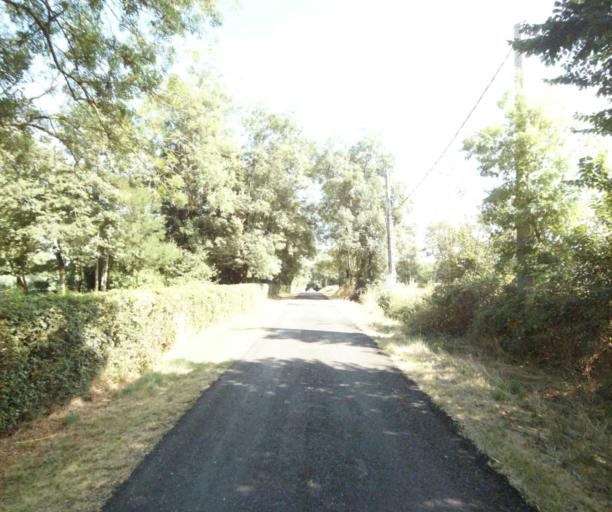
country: FR
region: Midi-Pyrenees
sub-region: Departement du Tarn
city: Soreze
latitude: 43.5111
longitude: 2.0540
